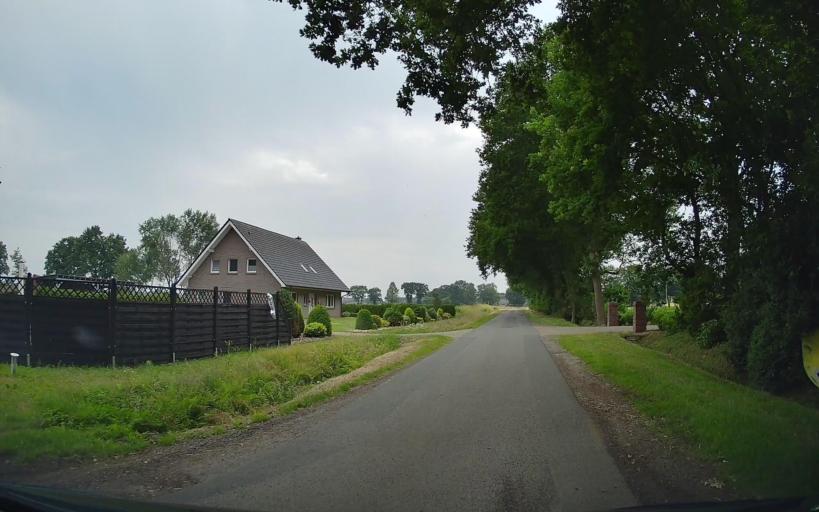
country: DE
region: Lower Saxony
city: Friesoythe
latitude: 53.0188
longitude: 7.9043
